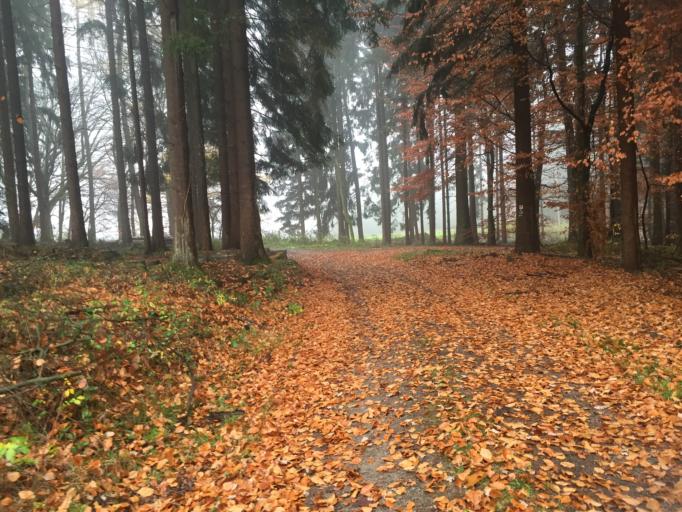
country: DE
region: Baden-Wuerttemberg
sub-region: Karlsruhe Region
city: Heddesbach
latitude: 49.4487
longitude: 8.8460
